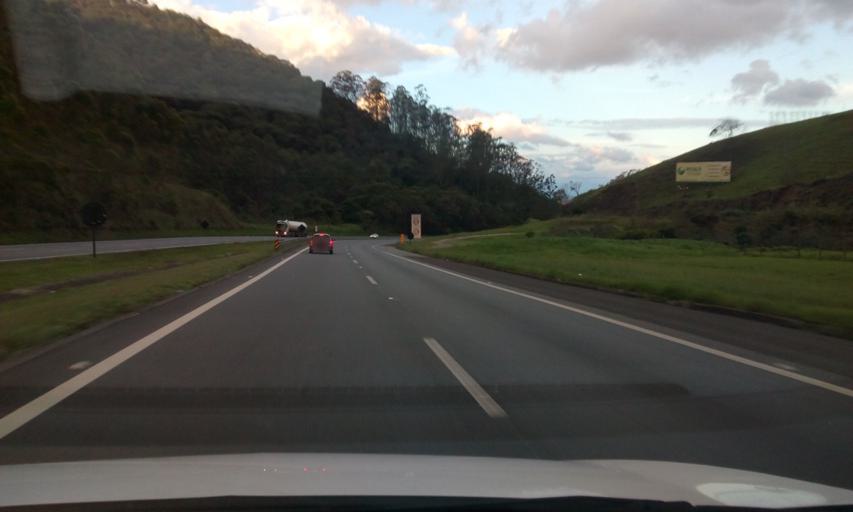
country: BR
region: Sao Paulo
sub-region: Santa Isabel
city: Santa Isabel
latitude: -23.1742
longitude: -46.2509
